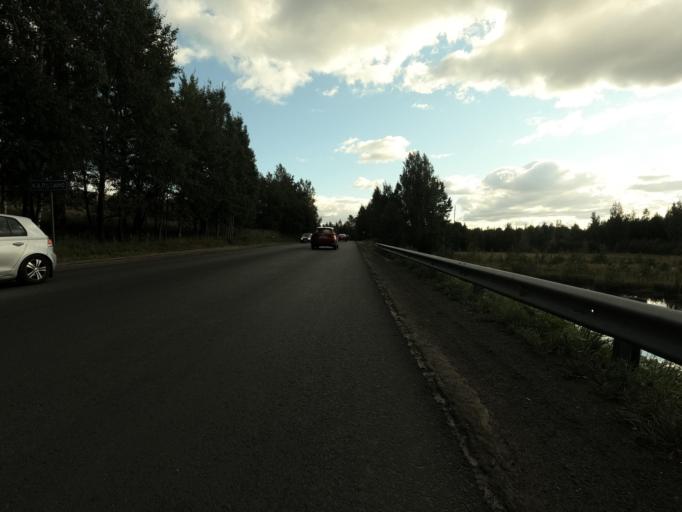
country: RU
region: Leningrad
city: Koltushi
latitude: 59.9729
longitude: 30.6531
